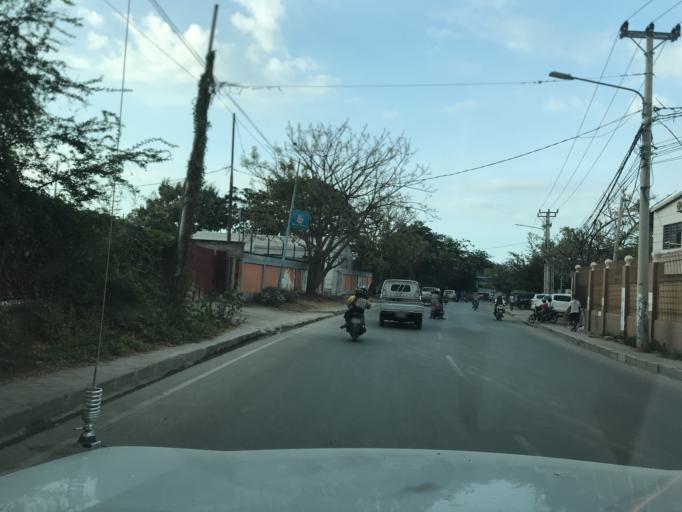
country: TL
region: Dili
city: Dili
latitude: -8.5485
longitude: 125.5434
